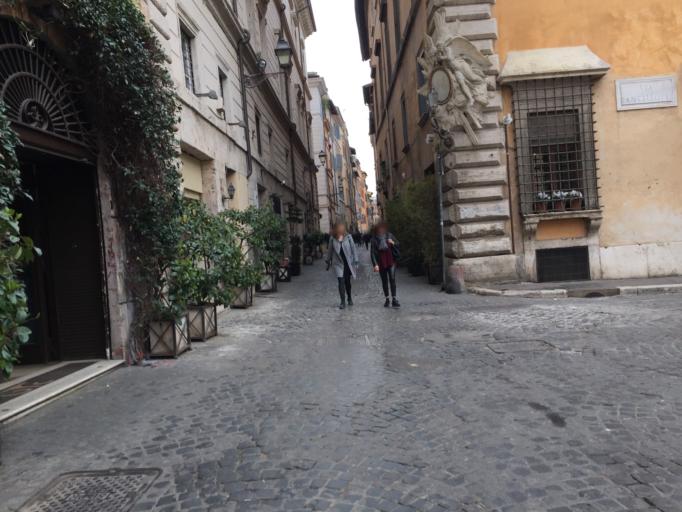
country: VA
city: Vatican City
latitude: 41.9006
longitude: 12.4708
